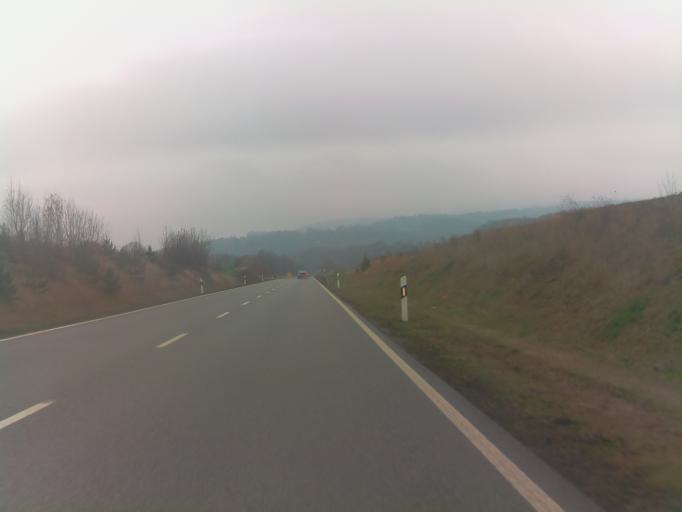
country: DE
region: Thuringia
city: Schleusingen
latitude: 50.4954
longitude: 10.7670
